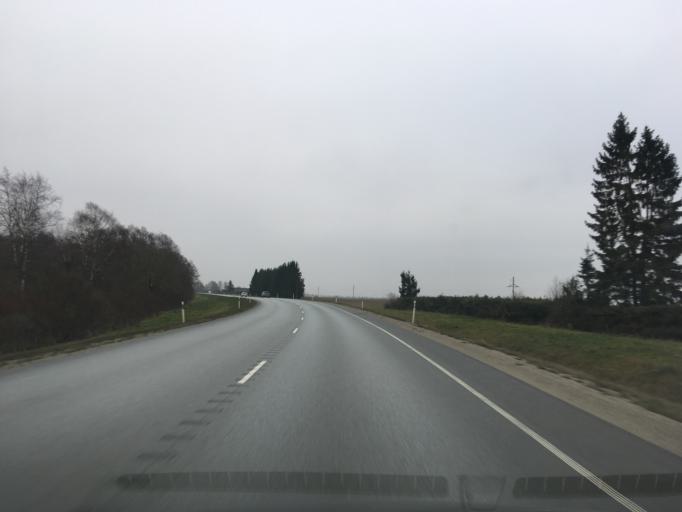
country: EE
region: Ida-Virumaa
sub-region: Kivioli linn
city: Kivioli
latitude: 59.4191
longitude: 26.9722
